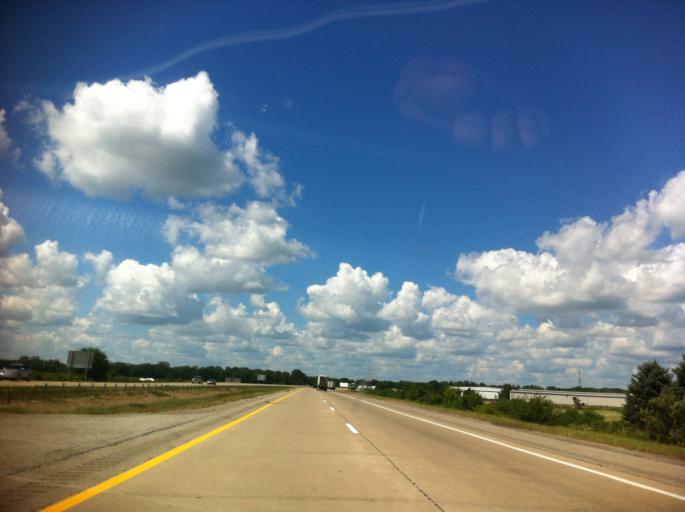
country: US
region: Michigan
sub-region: Monroe County
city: Dundee
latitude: 41.9694
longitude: -83.6752
